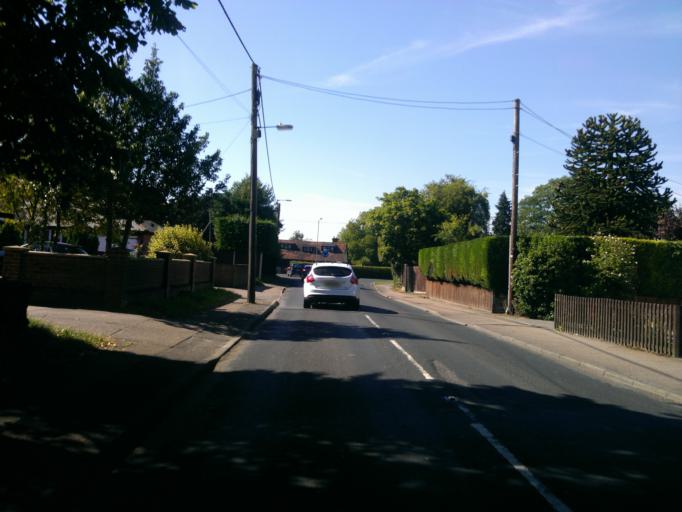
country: GB
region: England
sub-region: Essex
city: Layer de la Haye
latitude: 51.8641
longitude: 0.8731
